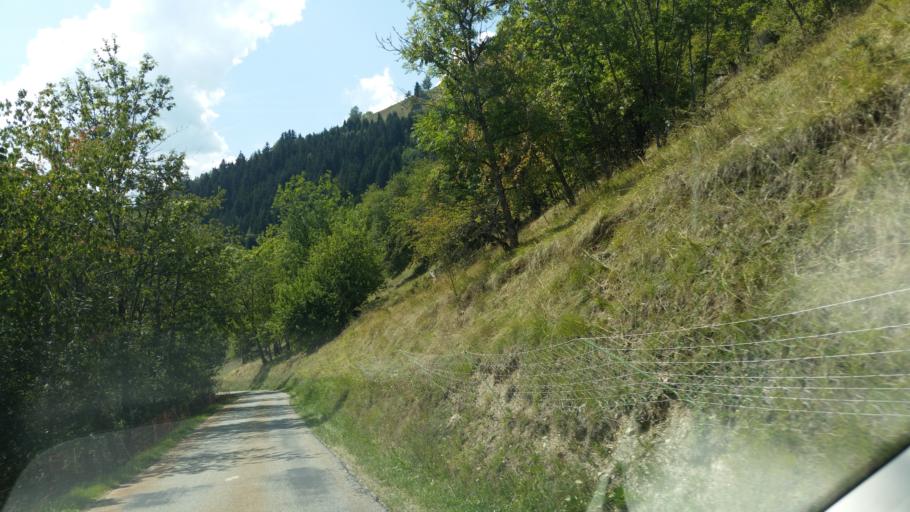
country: FR
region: Rhone-Alpes
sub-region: Departement de la Savoie
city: La Chambre
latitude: 45.3962
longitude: 6.3199
